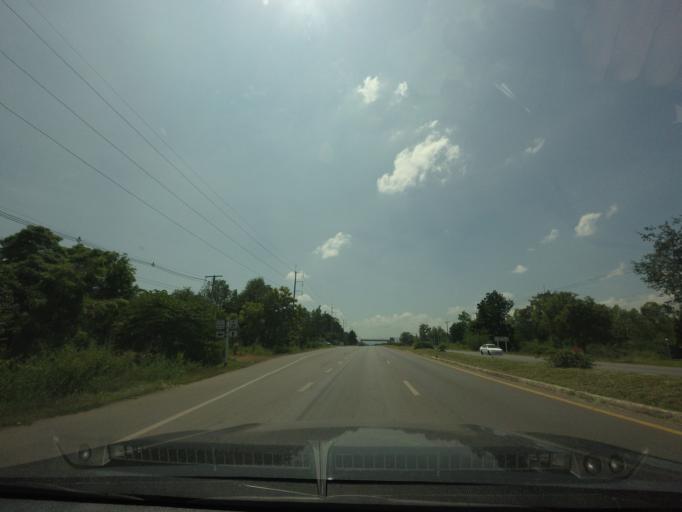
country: TH
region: Phetchabun
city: Lom Sak
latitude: 16.7291
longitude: 101.1883
